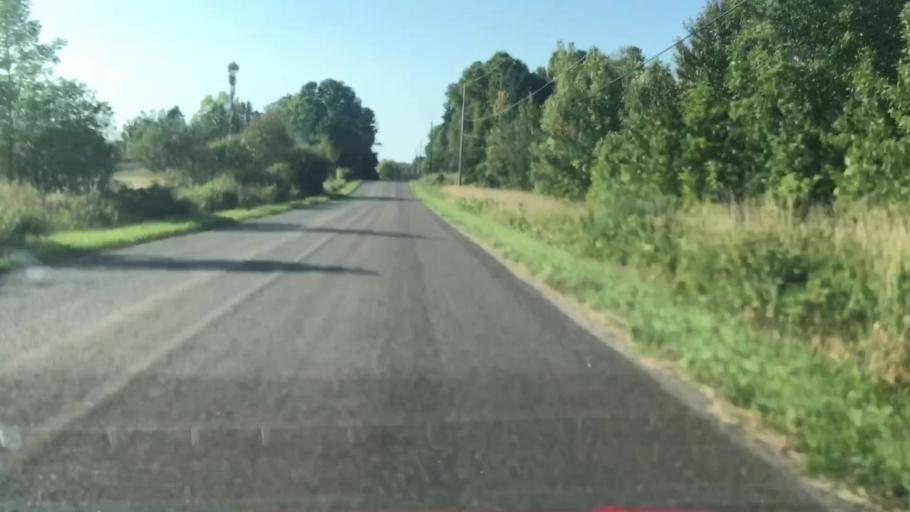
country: US
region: Michigan
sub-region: Chippewa County
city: Sault Ste. Marie
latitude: 46.2879
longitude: -84.0599
